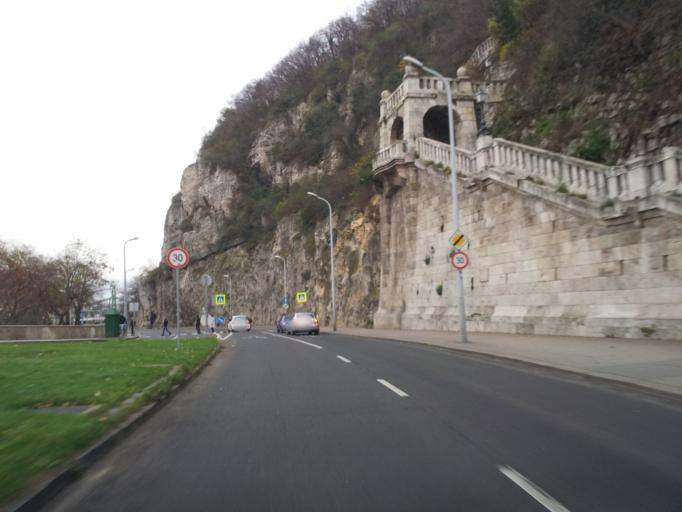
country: HU
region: Budapest
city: Budapest I. keruelet
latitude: 47.4898
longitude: 19.0460
